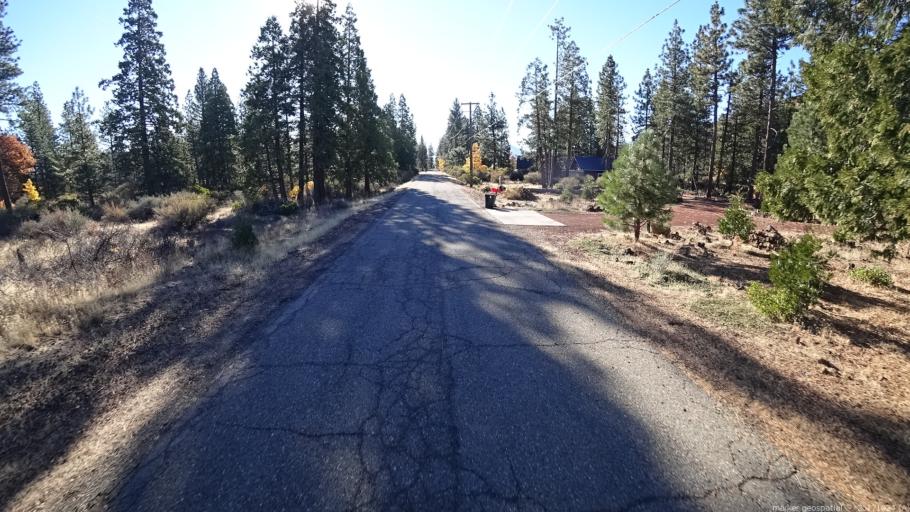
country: US
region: California
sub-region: Shasta County
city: Burney
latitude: 40.8400
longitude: -121.5158
